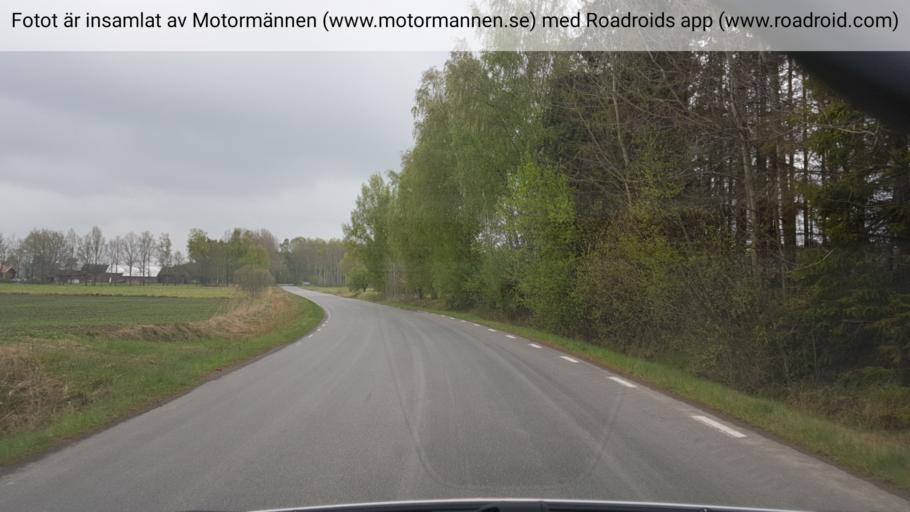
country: SE
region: Vaestra Goetaland
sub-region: Skovde Kommun
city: Stopen
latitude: 58.5641
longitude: 13.9837
